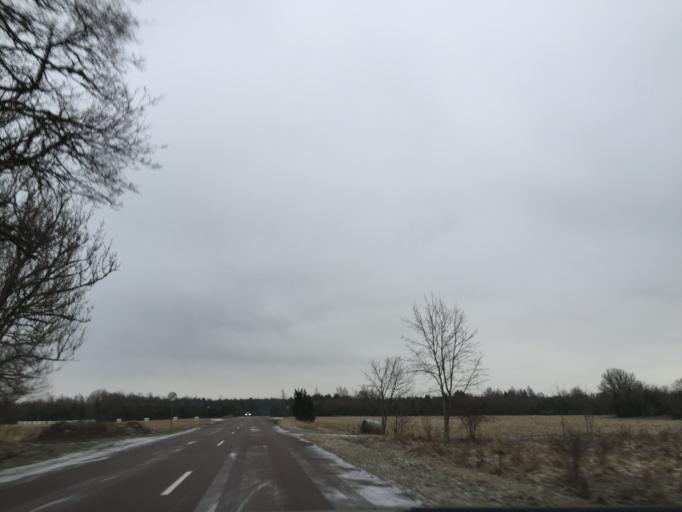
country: EE
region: Saare
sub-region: Orissaare vald
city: Orissaare
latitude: 58.6012
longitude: 23.1173
